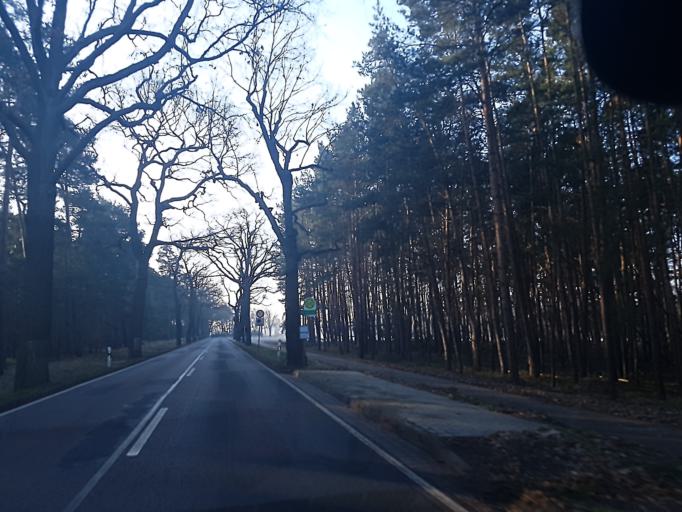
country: DE
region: Brandenburg
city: Golzow
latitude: 52.2580
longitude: 12.5986
